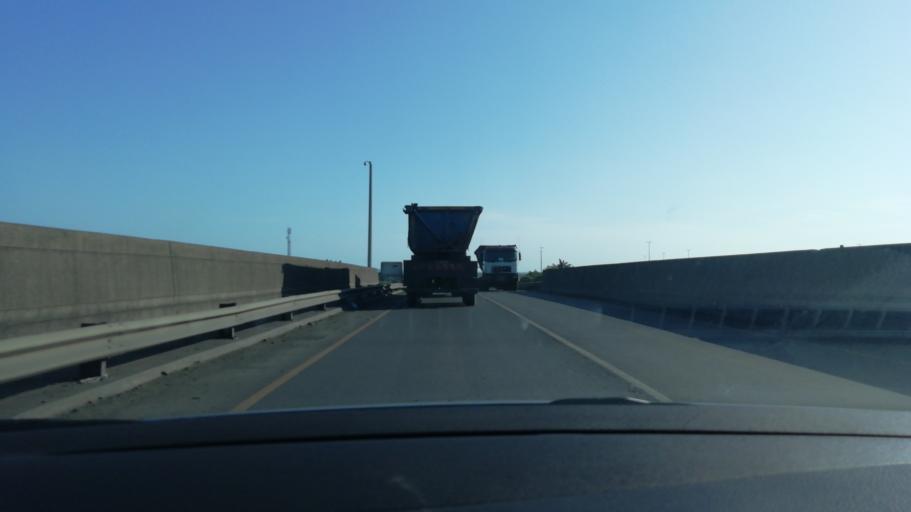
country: ZA
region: KwaZulu-Natal
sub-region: uThungulu District Municipality
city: Richards Bay
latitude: -28.7825
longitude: 32.0280
